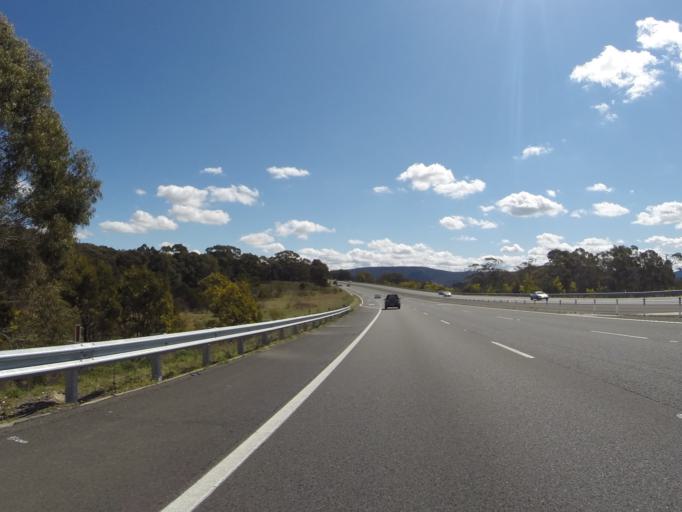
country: AU
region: New South Wales
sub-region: Goulburn Mulwaree
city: Goulburn
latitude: -34.7357
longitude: 149.8317
